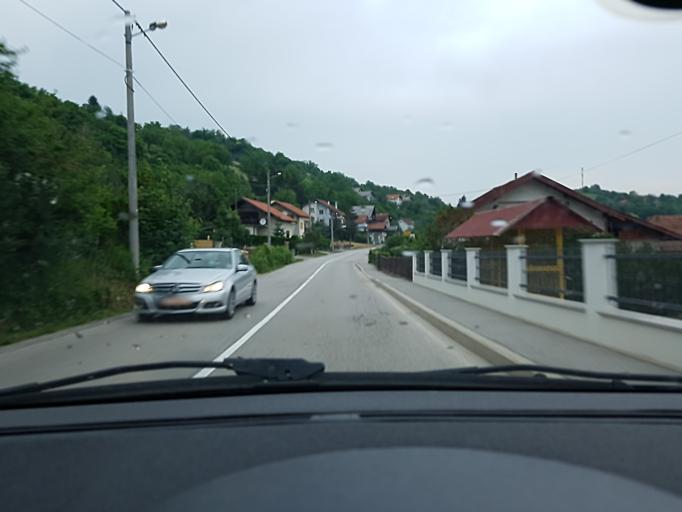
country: HR
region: Zagrebacka
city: Pojatno
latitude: 45.9197
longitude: 15.8074
